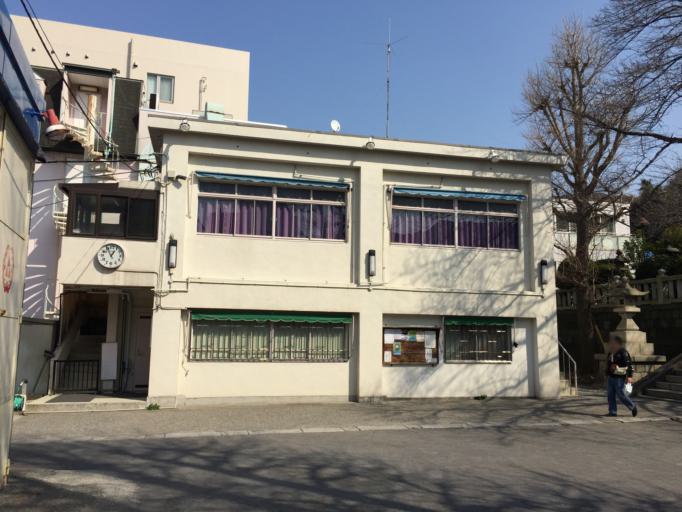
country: JP
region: Kanagawa
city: Yokohama
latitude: 35.4391
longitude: 139.6468
